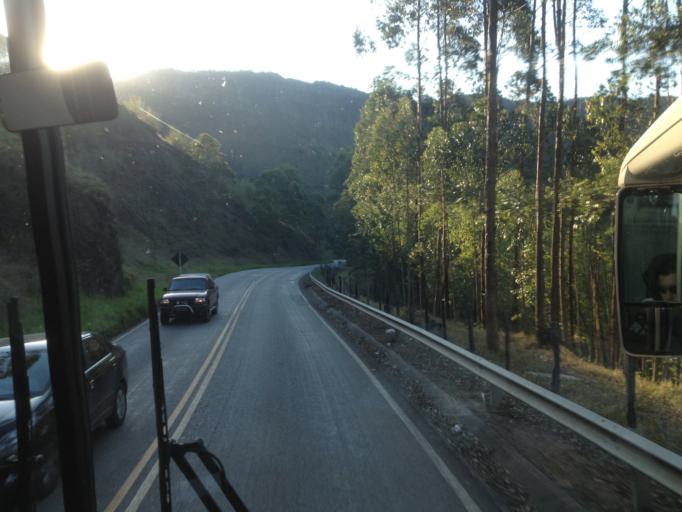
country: BR
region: Minas Gerais
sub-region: Juiz De Fora
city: Juiz de Fora
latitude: -21.6551
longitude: -43.3292
